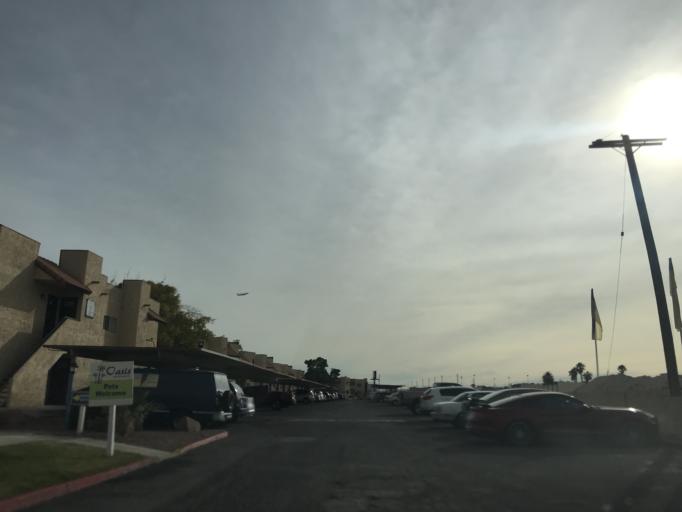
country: US
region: Nevada
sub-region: Clark County
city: Paradise
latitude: 36.0934
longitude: -115.1698
